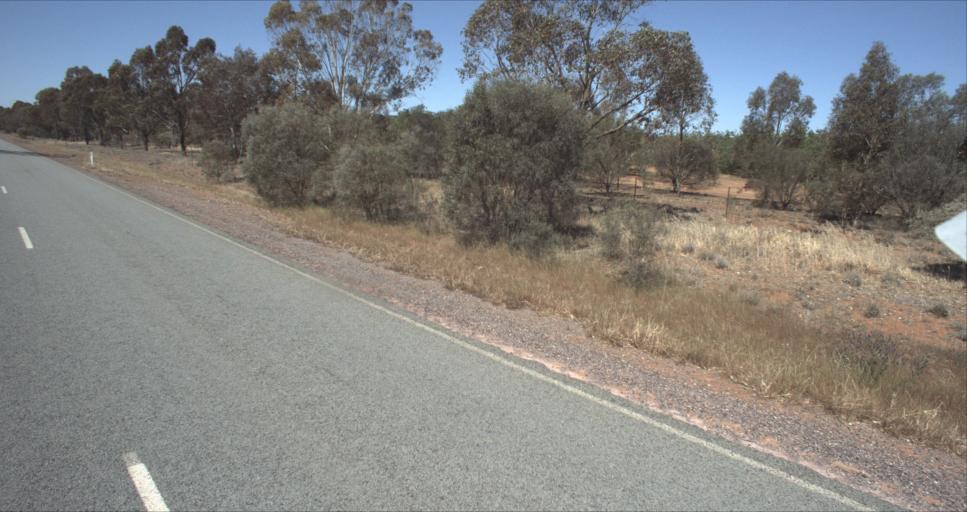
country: AU
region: New South Wales
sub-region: Leeton
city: Leeton
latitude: -34.4928
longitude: 146.4616
